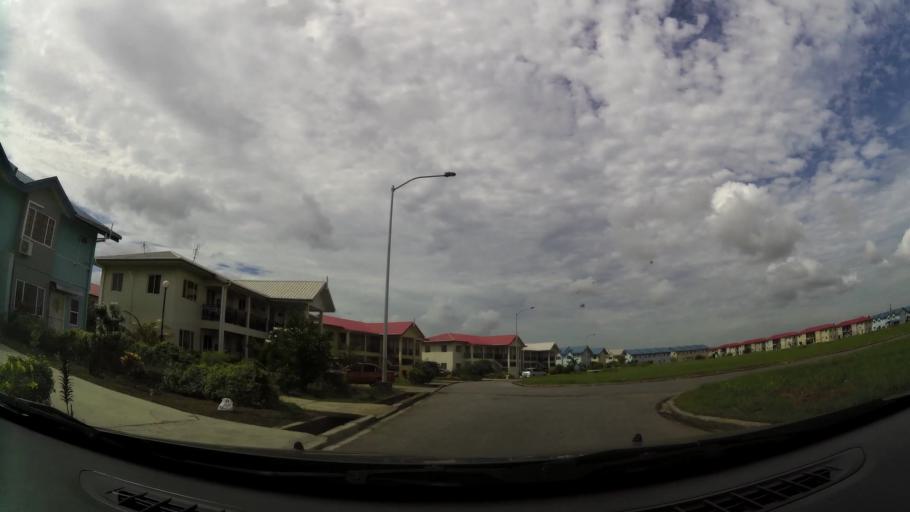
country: TT
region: Chaguanas
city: Chaguanas
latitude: 10.5036
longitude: -61.3974
